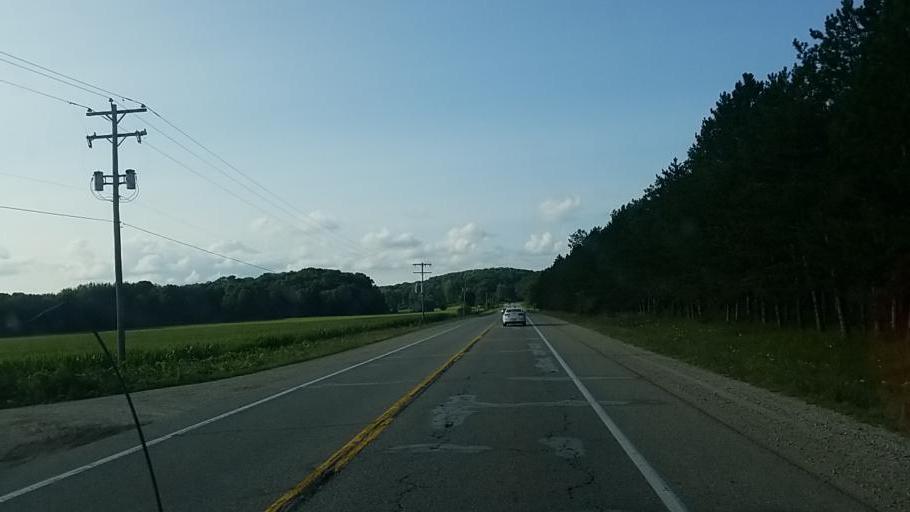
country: US
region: Michigan
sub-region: Kent County
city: Lowell
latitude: 42.9610
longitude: -85.3554
